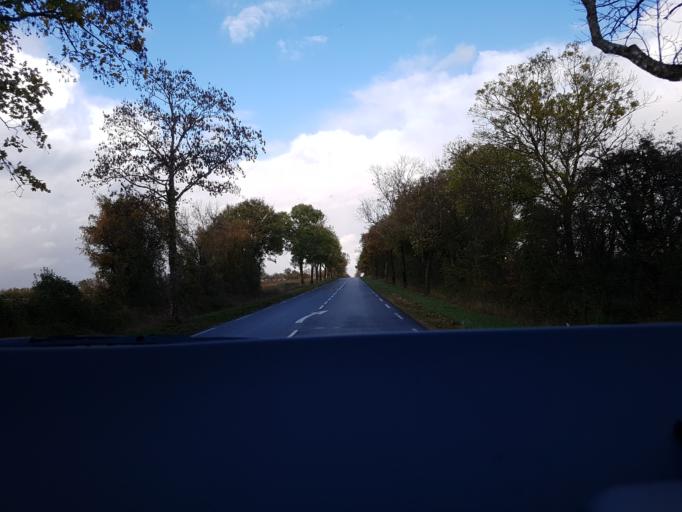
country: FR
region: Poitou-Charentes
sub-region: Departement des Deux-Sevres
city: Brioux-sur-Boutonne
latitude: 46.1034
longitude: -0.2661
